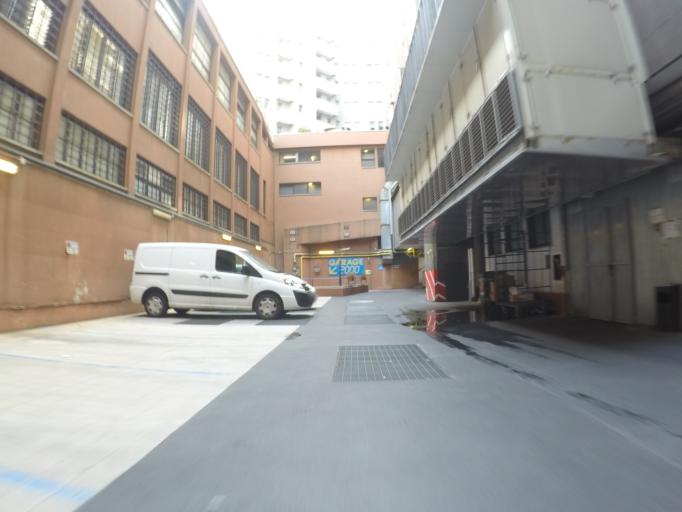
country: IT
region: Lombardy
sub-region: Citta metropolitana di Milano
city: Milano
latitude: 45.4838
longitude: 9.2010
